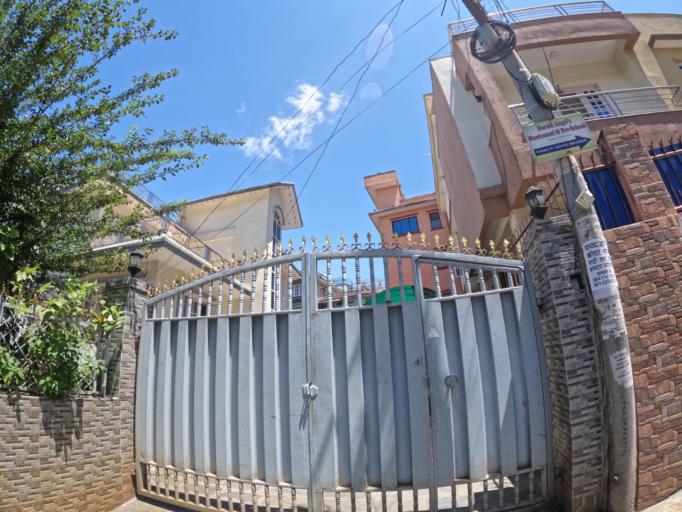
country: NP
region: Central Region
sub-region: Bagmati Zone
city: Kathmandu
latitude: 27.7451
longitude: 85.3259
